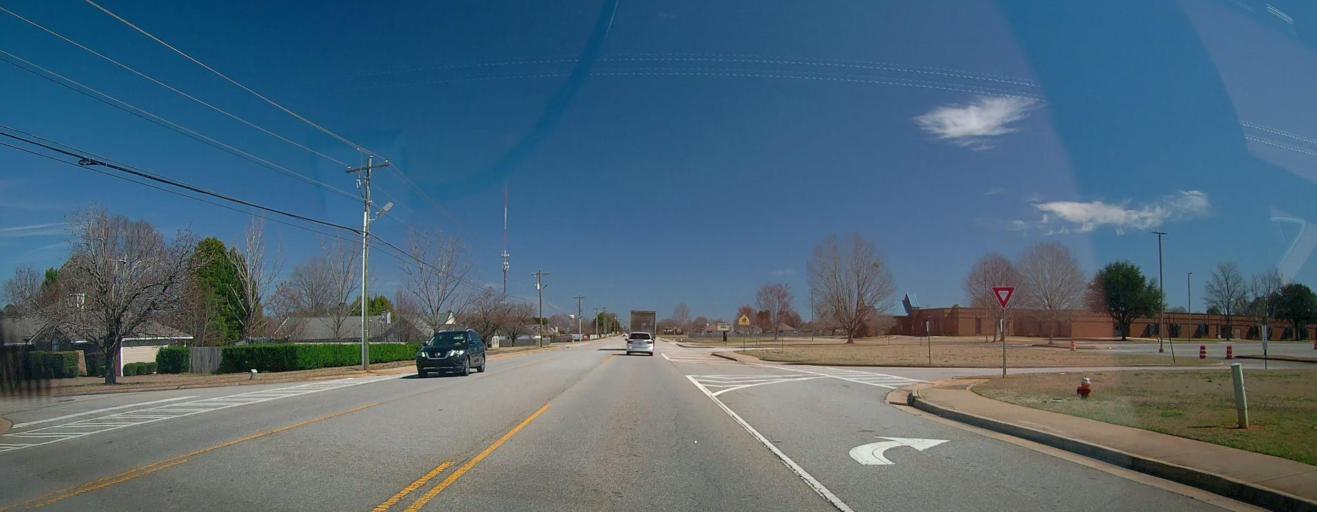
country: US
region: Georgia
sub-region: Houston County
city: Centerville
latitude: 32.5709
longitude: -83.6778
